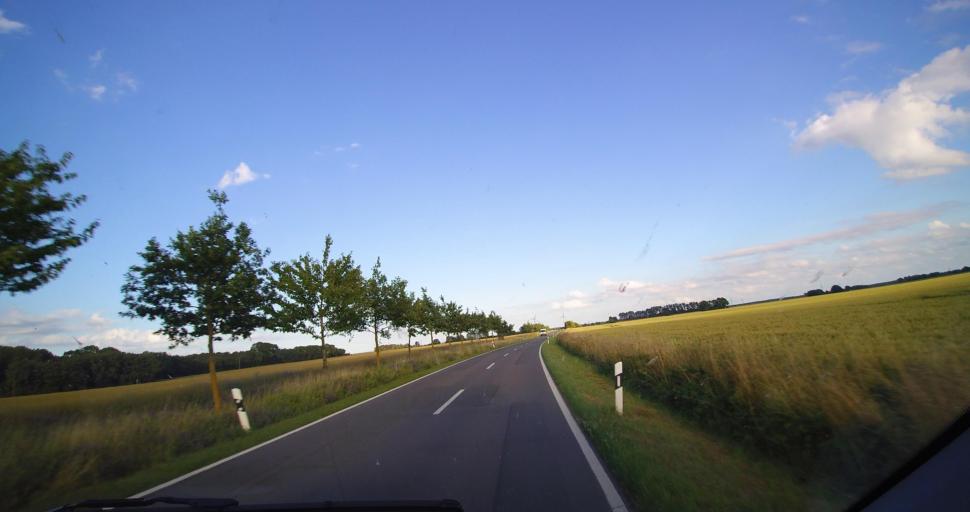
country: DE
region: Mecklenburg-Vorpommern
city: Franzburg
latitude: 54.2191
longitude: 12.8509
